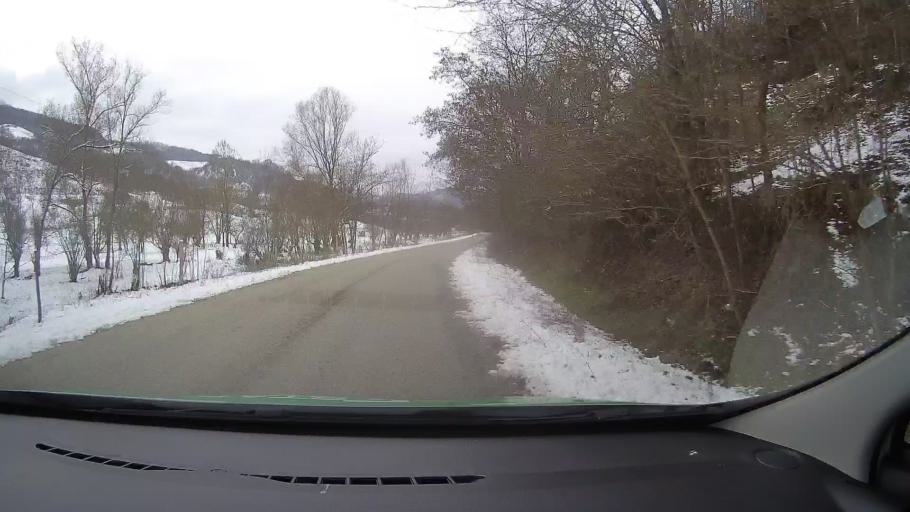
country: RO
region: Hunedoara
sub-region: Comuna Balsa
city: Balsa
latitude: 46.0579
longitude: 23.0917
